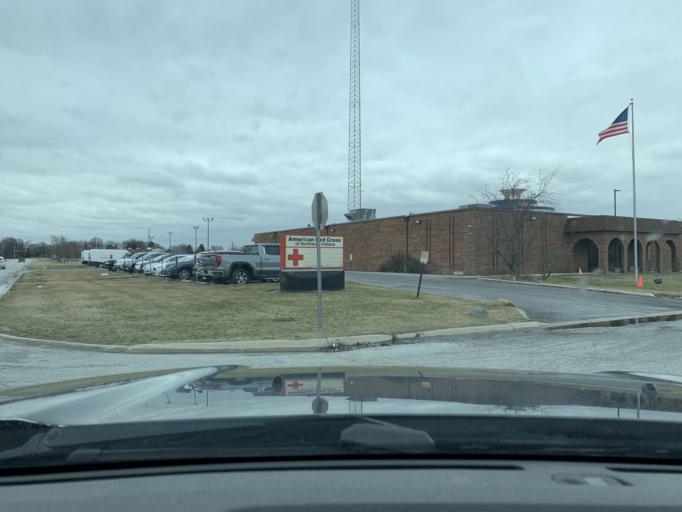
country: US
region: Indiana
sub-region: Lake County
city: Merrillville
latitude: 41.4675
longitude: -87.3263
